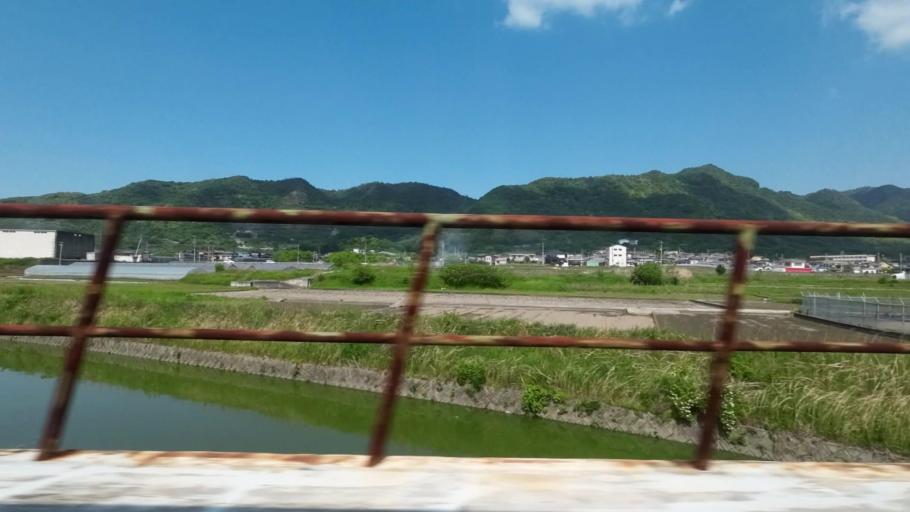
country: JP
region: Kagawa
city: Kan'onjicho
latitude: 34.1493
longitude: 133.6869
